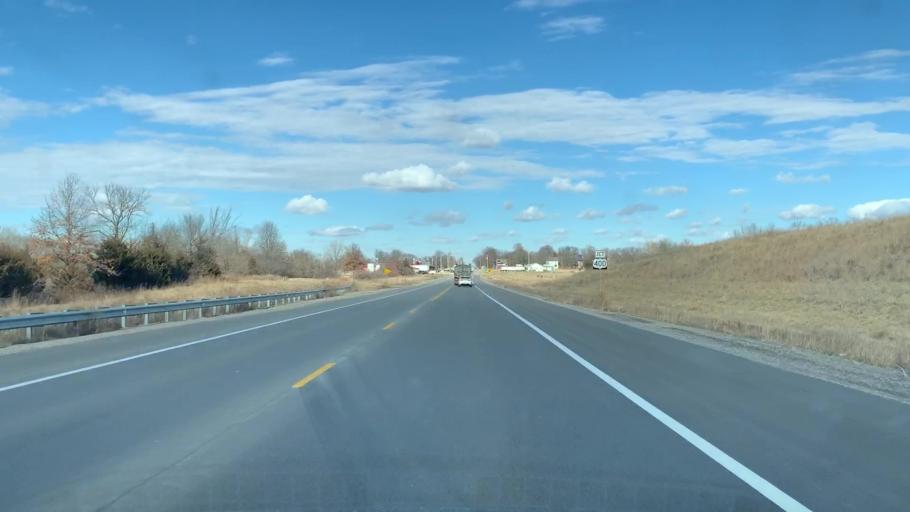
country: US
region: Kansas
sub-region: Crawford County
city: Pittsburg
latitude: 37.3356
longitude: -94.8322
